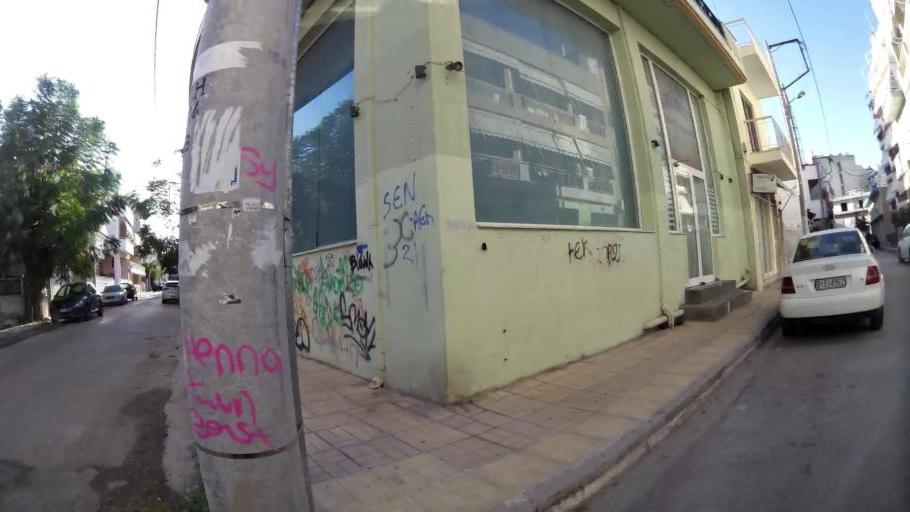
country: GR
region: Attica
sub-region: Nomarchia Anatolikis Attikis
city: Acharnes
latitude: 38.0774
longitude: 23.7410
